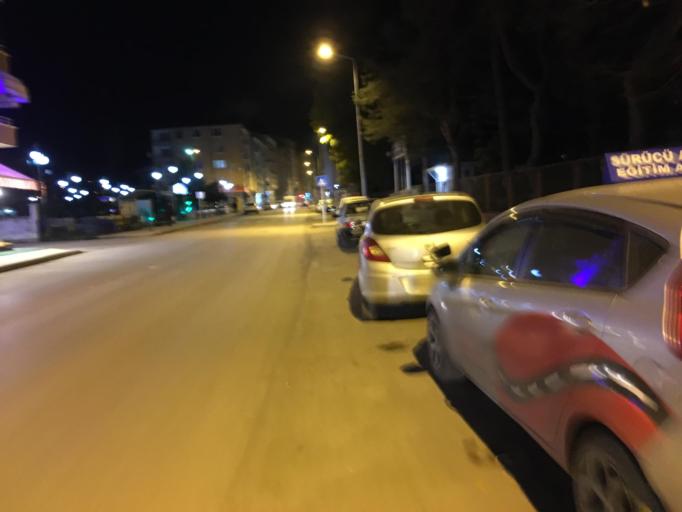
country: TR
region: Samsun
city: Alacam
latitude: 41.6123
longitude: 35.6046
